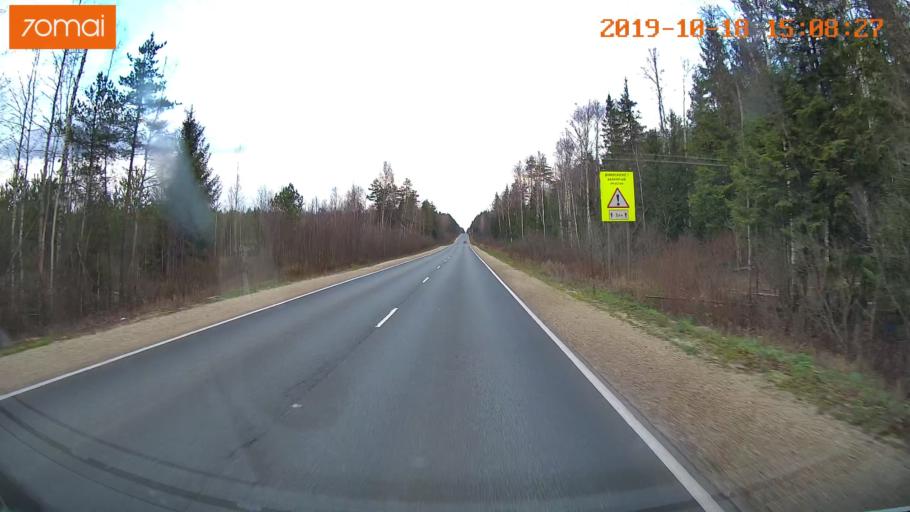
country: RU
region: Vladimir
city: Gus'-Khrustal'nyy
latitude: 55.5525
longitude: 40.6107
